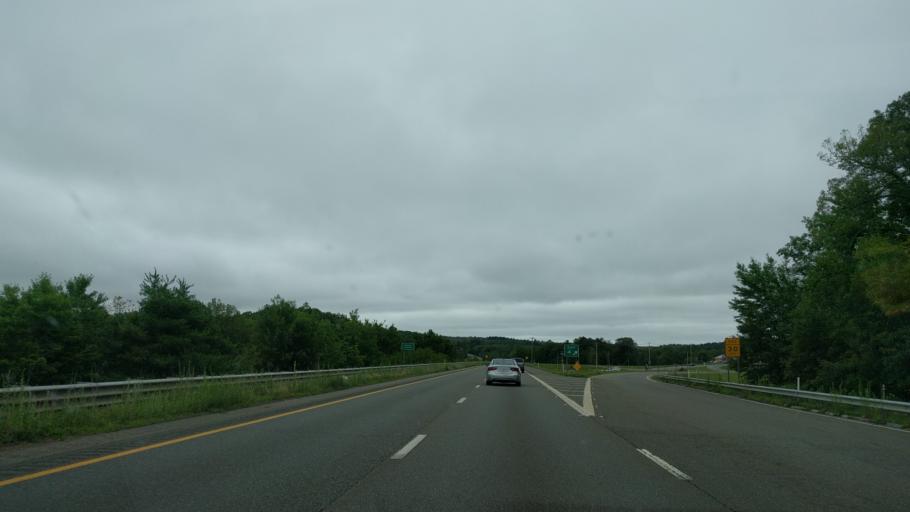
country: US
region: Massachusetts
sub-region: Worcester County
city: East Douglas
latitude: 42.0915
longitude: -71.6971
